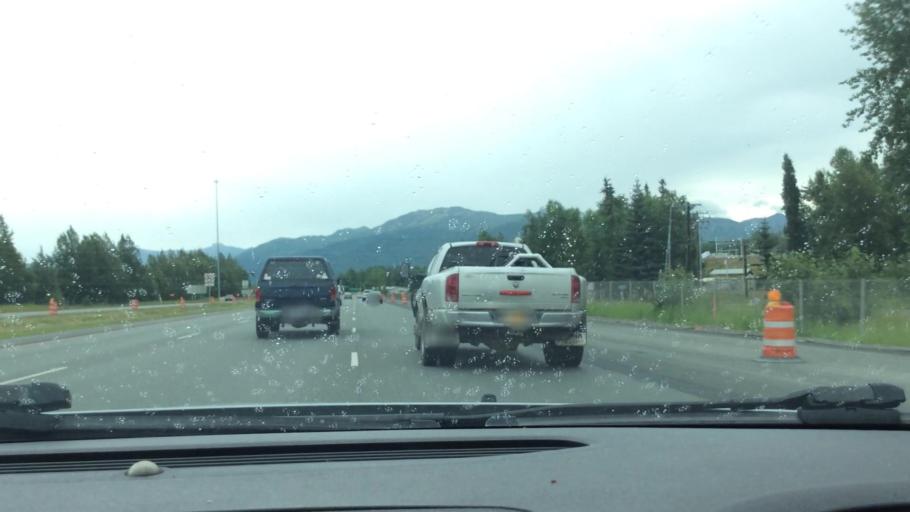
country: US
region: Alaska
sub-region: Anchorage Municipality
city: Elmendorf Air Force Base
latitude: 61.2288
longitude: -149.7240
